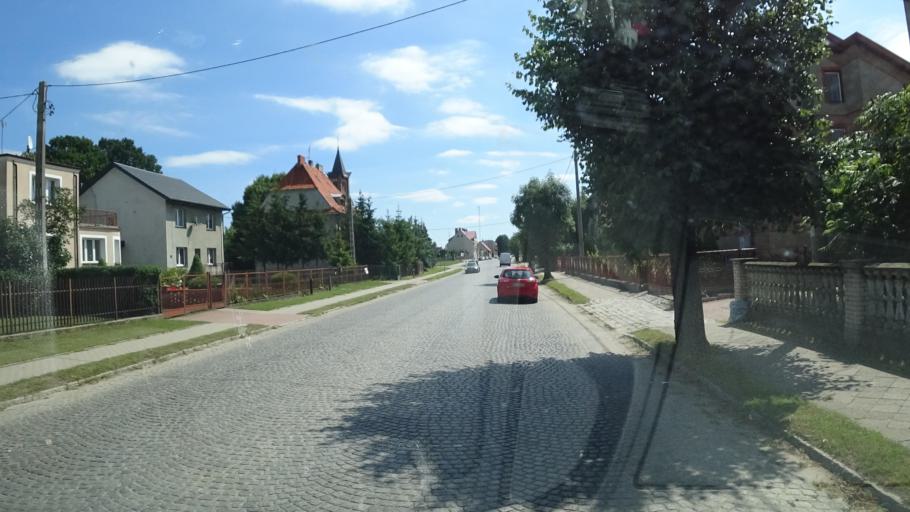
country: PL
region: Warmian-Masurian Voivodeship
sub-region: Powiat elcki
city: Prostki
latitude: 53.6992
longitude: 22.4313
